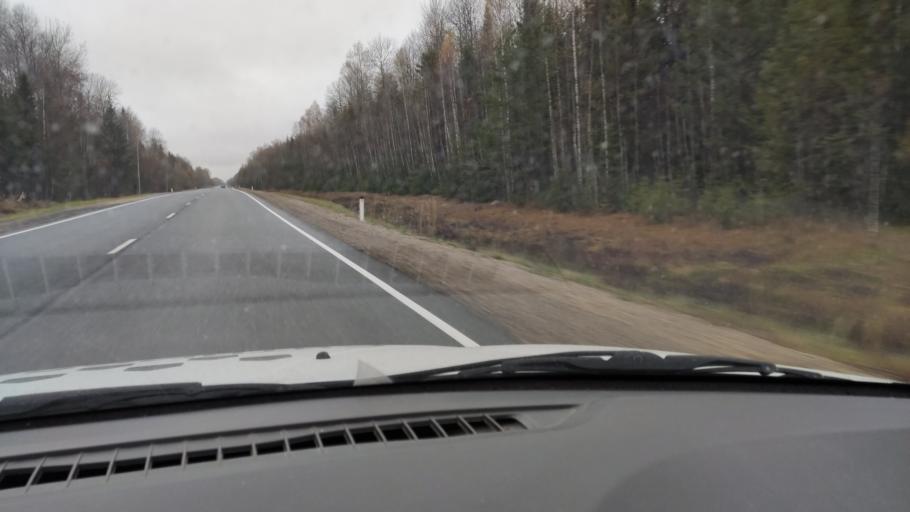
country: RU
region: Kirov
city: Chernaya Kholunitsa
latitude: 58.7789
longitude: 51.9192
